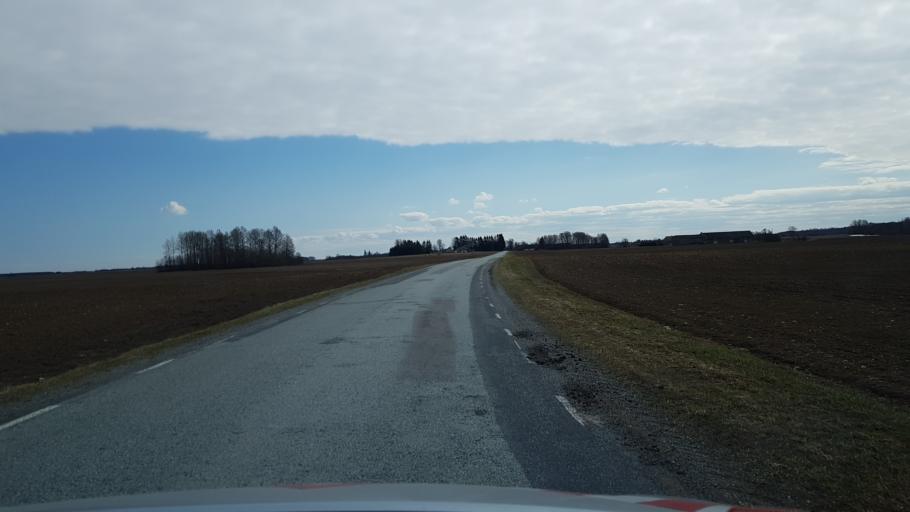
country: EE
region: Laeaene-Virumaa
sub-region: Haljala vald
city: Haljala
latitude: 59.4233
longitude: 26.2308
